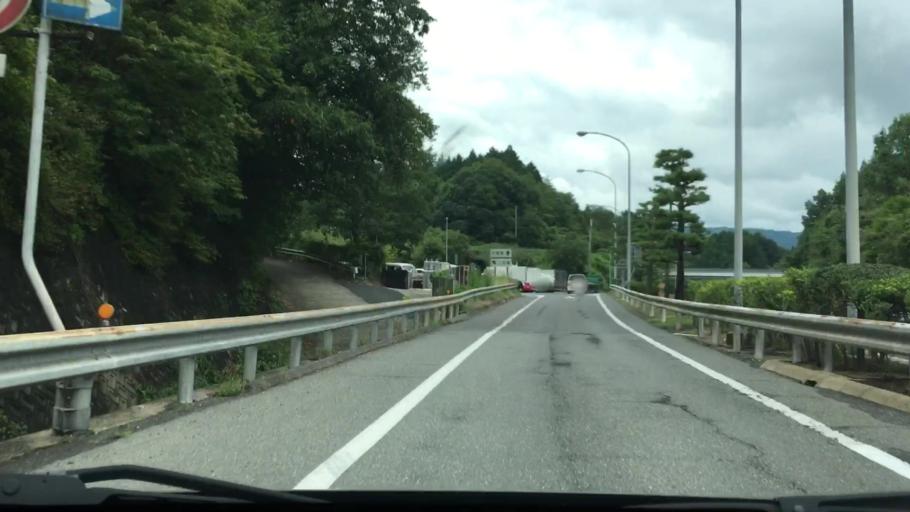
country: JP
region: Okayama
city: Takahashi
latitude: 35.0104
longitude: 133.7299
